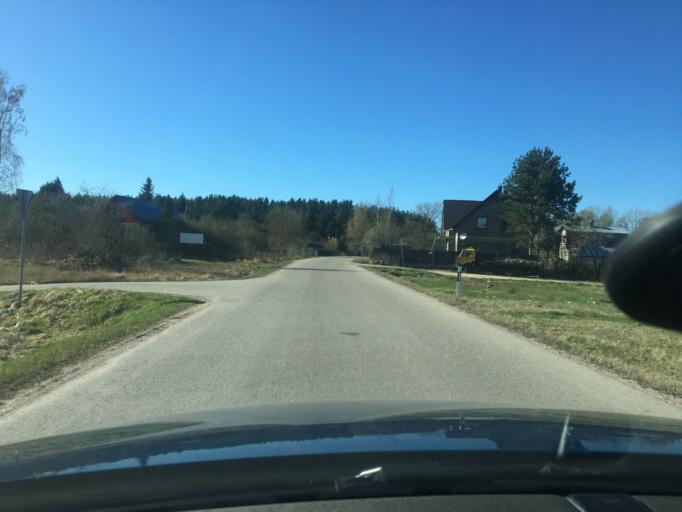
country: LV
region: Kekava
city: Kekava
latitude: 56.8531
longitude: 24.2580
